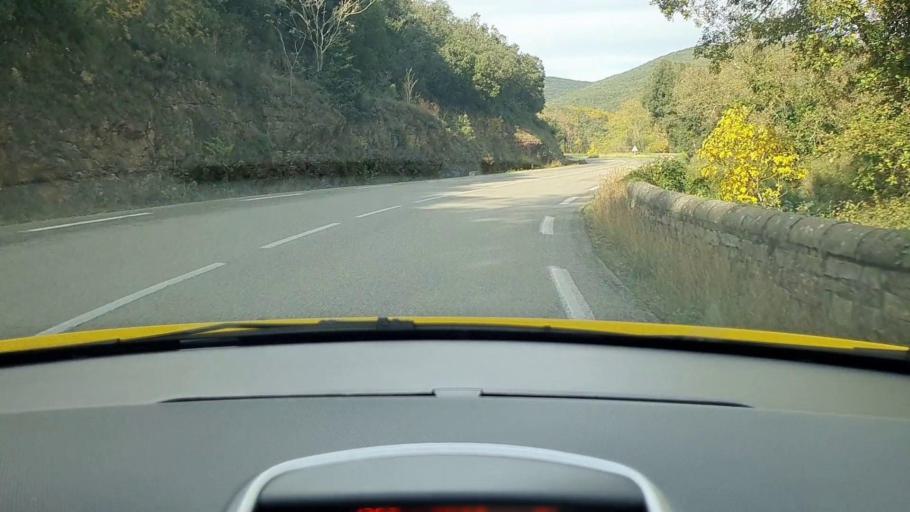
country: FR
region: Languedoc-Roussillon
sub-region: Departement du Gard
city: Anduze
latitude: 44.0688
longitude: 3.9350
